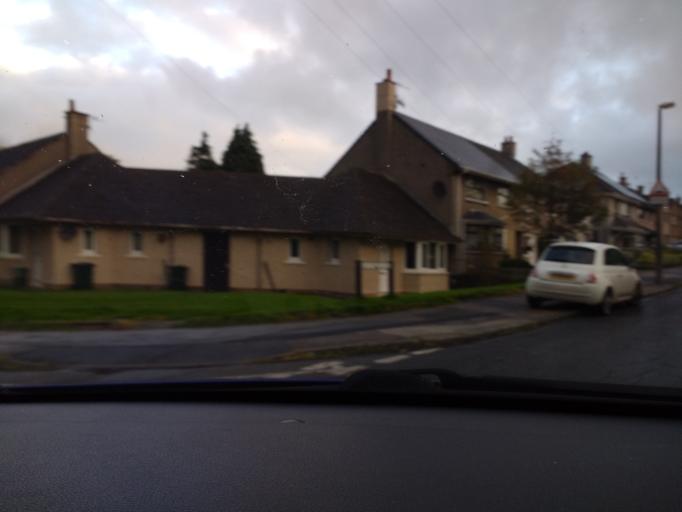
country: GB
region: England
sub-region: Lancashire
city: Lancaster
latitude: 54.0515
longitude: -2.7907
